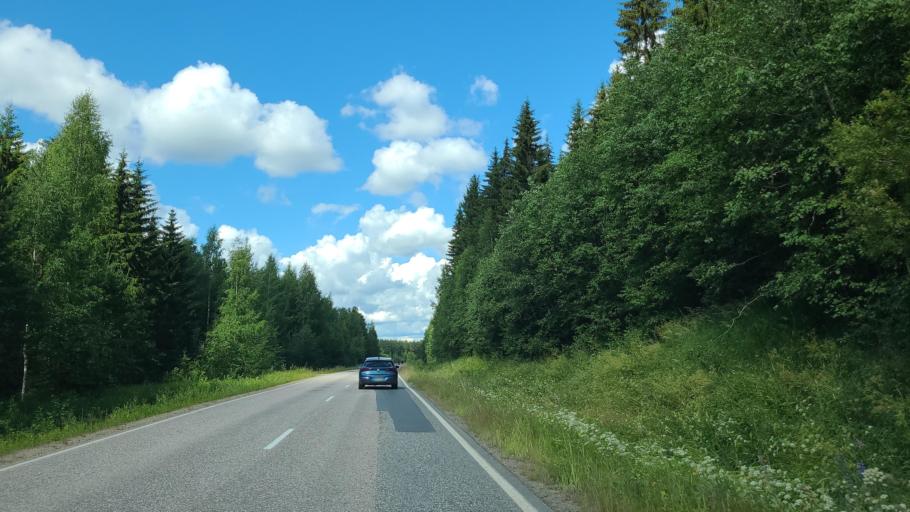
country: FI
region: Northern Savo
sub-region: Koillis-Savo
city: Kaavi
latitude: 62.9078
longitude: 28.7175
